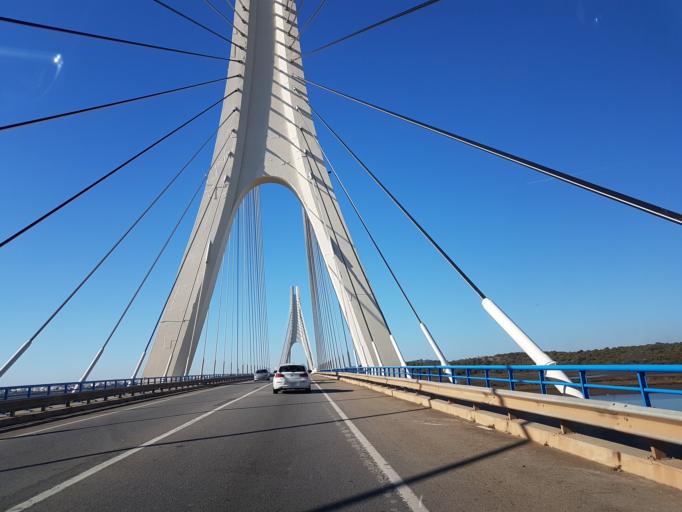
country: PT
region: Faro
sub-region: Lagoa
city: Estombar
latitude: 37.1513
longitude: -8.5046
